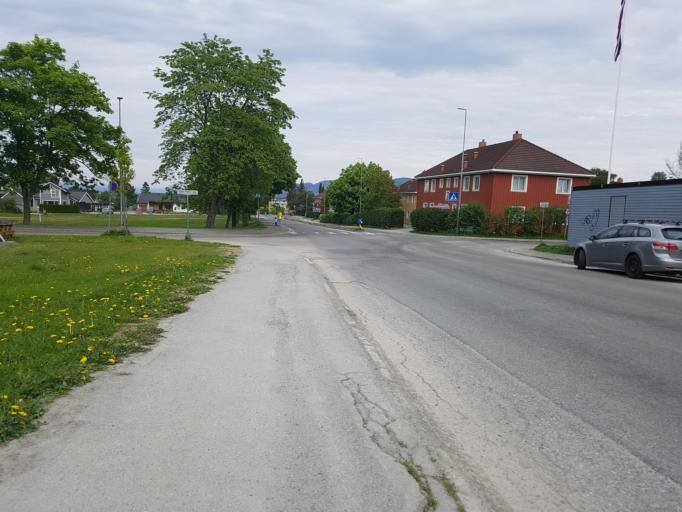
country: NO
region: Sor-Trondelag
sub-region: Trondheim
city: Trondheim
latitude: 63.4274
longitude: 10.4361
